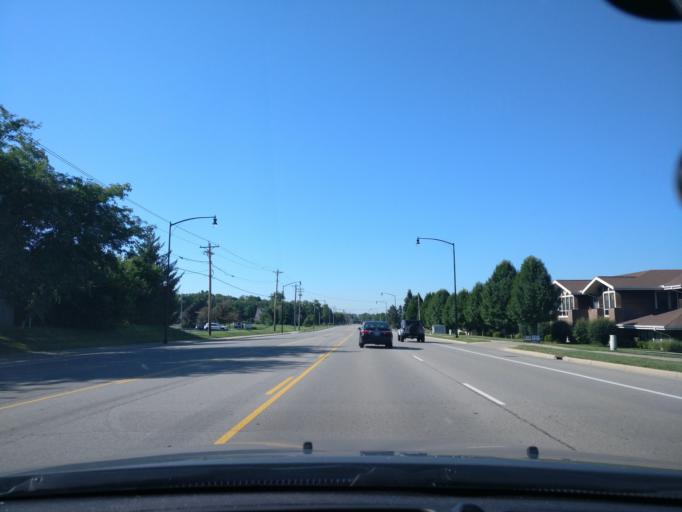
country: US
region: Ohio
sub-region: Warren County
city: Springboro
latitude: 39.5646
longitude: -84.2322
